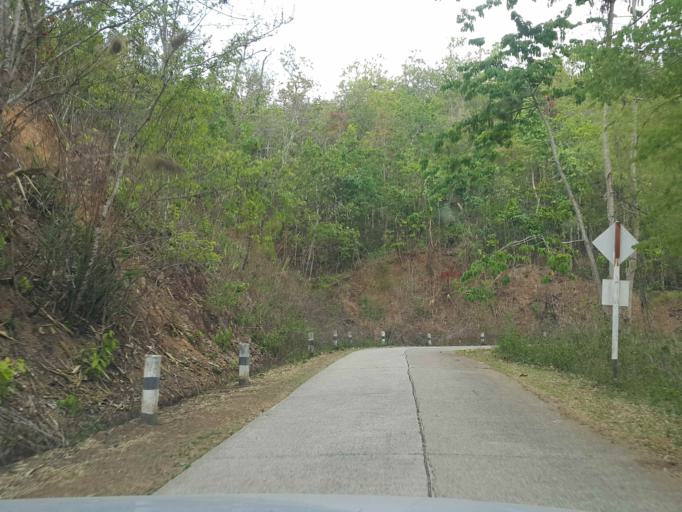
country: TH
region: Chiang Mai
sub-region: Amphoe Chiang Dao
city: Chiang Dao
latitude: 19.3788
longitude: 98.7662
